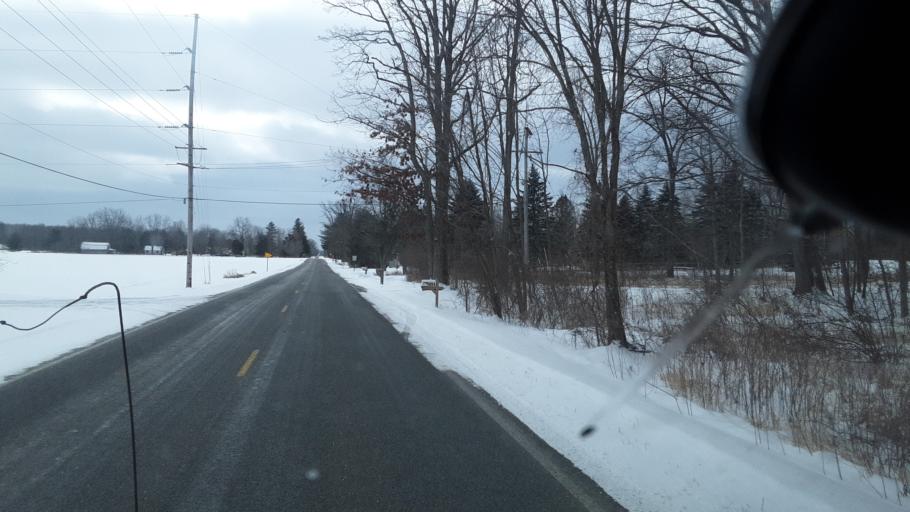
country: US
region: Michigan
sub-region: Ingham County
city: Holt
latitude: 42.6117
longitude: -84.5428
